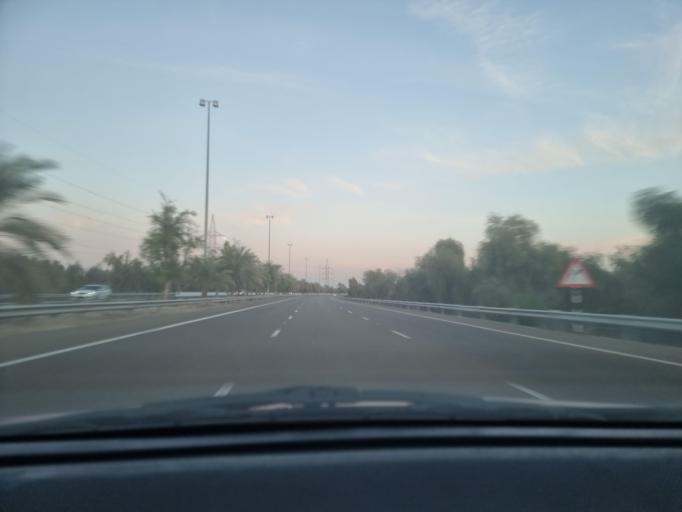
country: AE
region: Abu Dhabi
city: Al Ain
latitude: 24.1712
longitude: 55.2286
